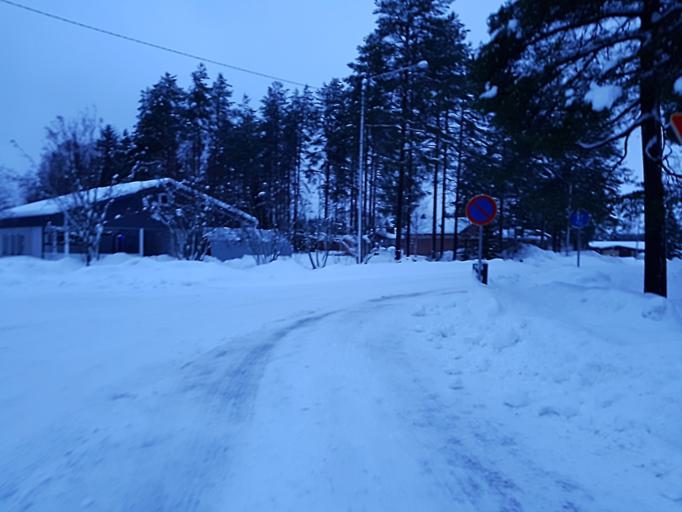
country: FI
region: Kainuu
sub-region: Kehys-Kainuu
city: Kuhmo
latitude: 64.1176
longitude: 29.5168
